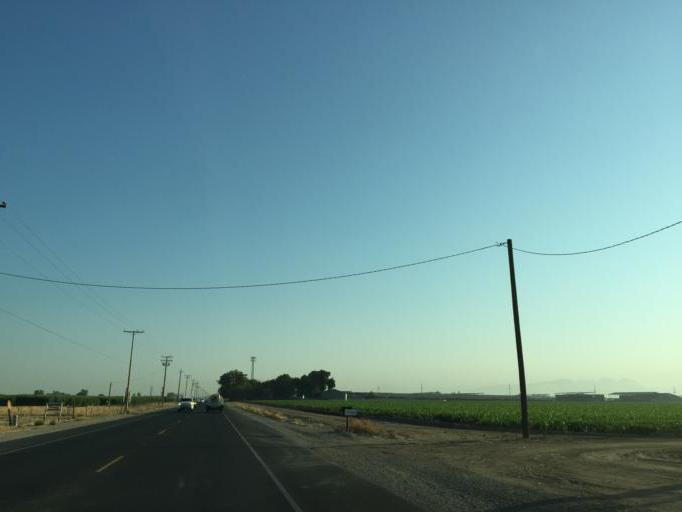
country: US
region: California
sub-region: Tulare County
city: Visalia
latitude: 36.4092
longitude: -119.2961
